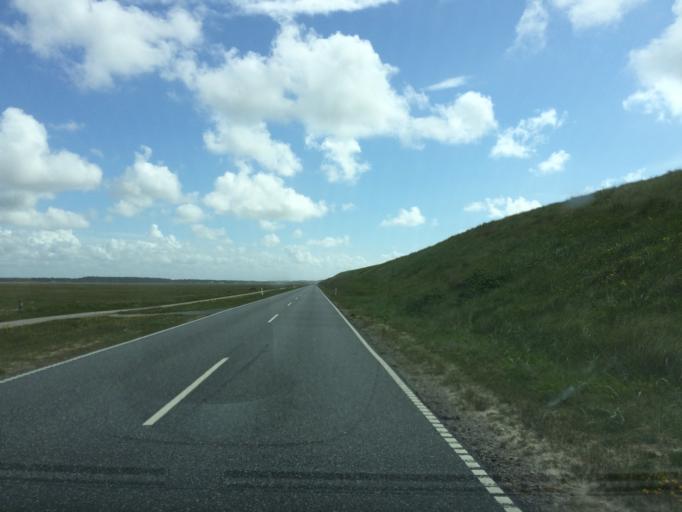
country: DK
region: Central Jutland
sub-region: Holstebro Kommune
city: Ulfborg
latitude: 56.3394
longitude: 8.1227
